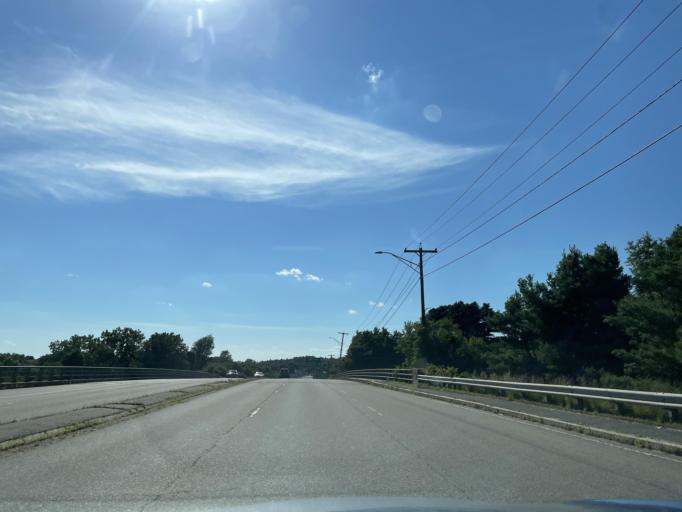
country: US
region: Massachusetts
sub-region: Worcester County
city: Oxford
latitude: 42.1165
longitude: -71.8540
